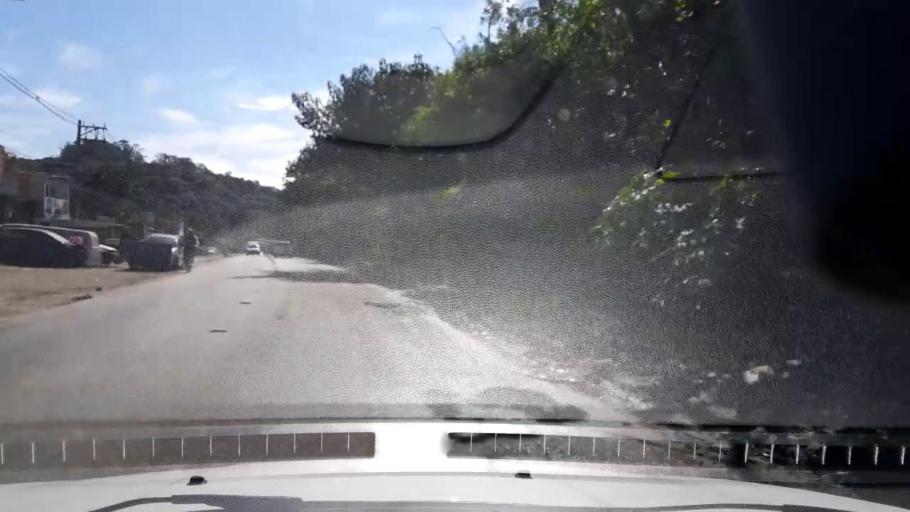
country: BR
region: Sao Paulo
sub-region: Ferraz De Vasconcelos
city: Ferraz de Vasconcelos
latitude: -23.5792
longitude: -46.4153
